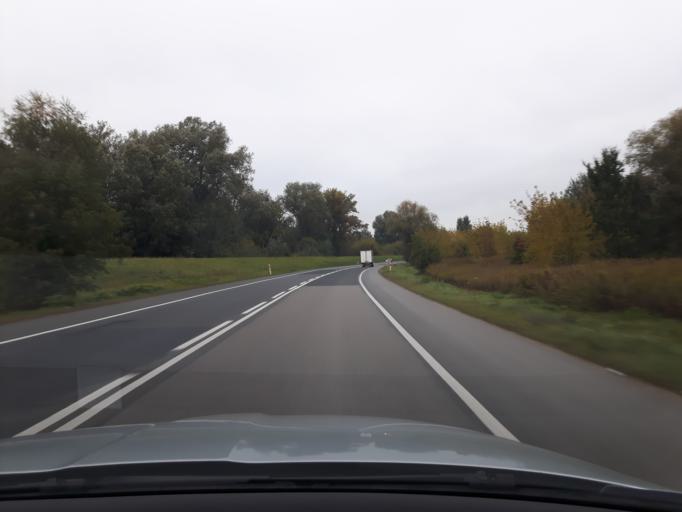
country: PL
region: Masovian Voivodeship
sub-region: Powiat nowodworski
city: Nowy Dwor Mazowiecki
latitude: 52.4188
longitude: 20.7096
